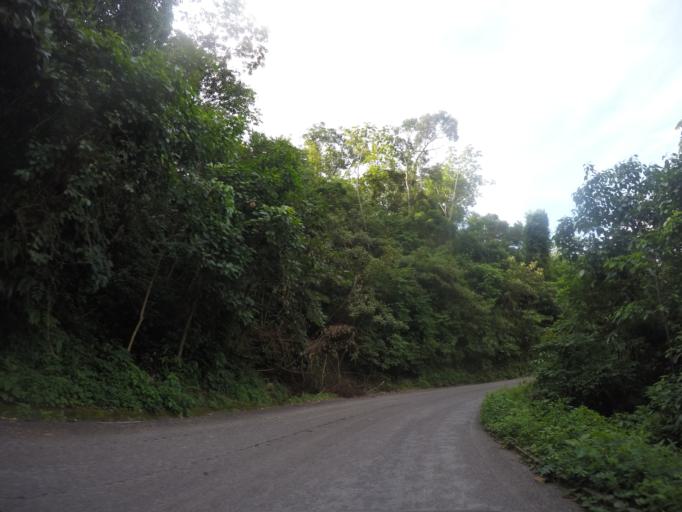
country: MX
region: Oaxaca
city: Pluma Hidalgo
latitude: 15.9394
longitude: -96.4380
